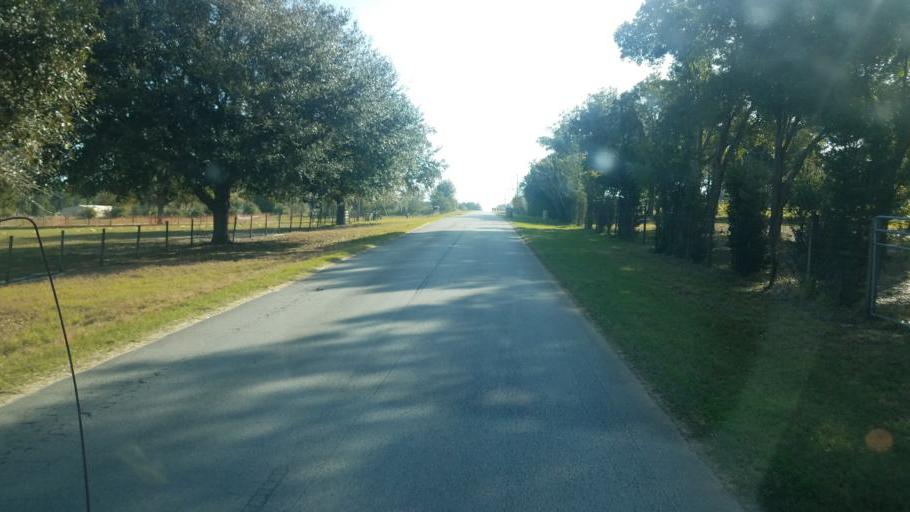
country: US
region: Florida
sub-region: Lake County
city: Clermont
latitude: 28.4615
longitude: -81.7827
